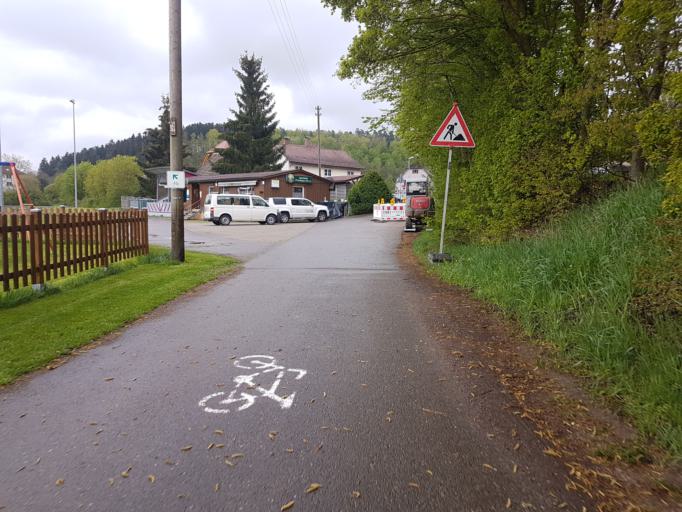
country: DE
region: Baden-Wuerttemberg
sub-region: Freiburg Region
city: Muhlheim am Bach
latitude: 48.3858
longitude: 8.6773
